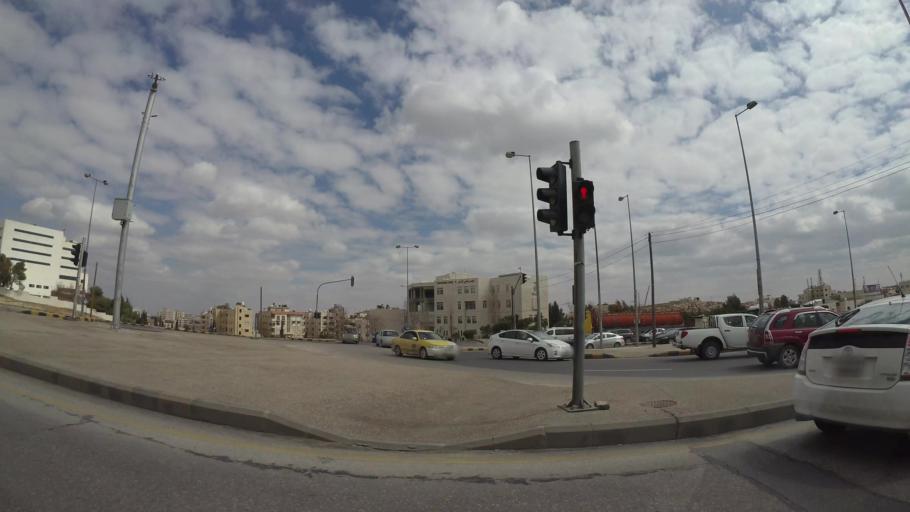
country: JO
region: Amman
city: Amman
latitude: 31.9983
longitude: 35.9180
